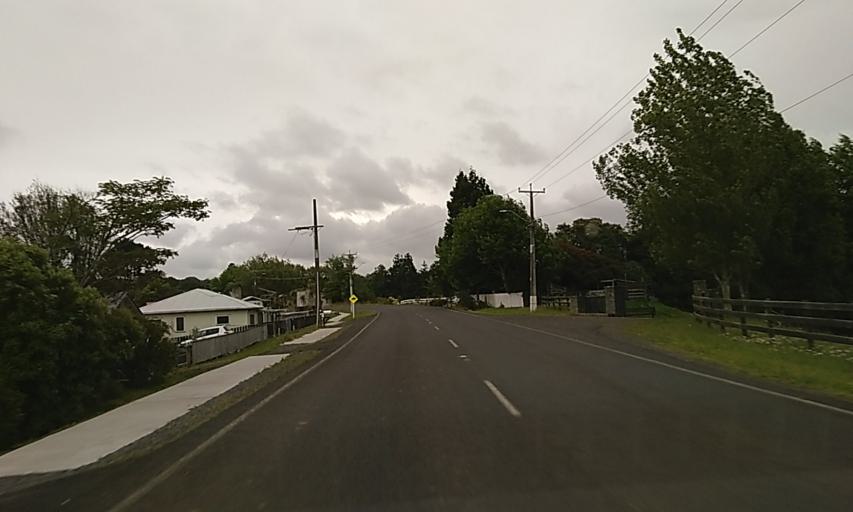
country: NZ
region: Auckland
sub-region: Auckland
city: Pukekohe East
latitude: -37.3255
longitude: 174.9171
